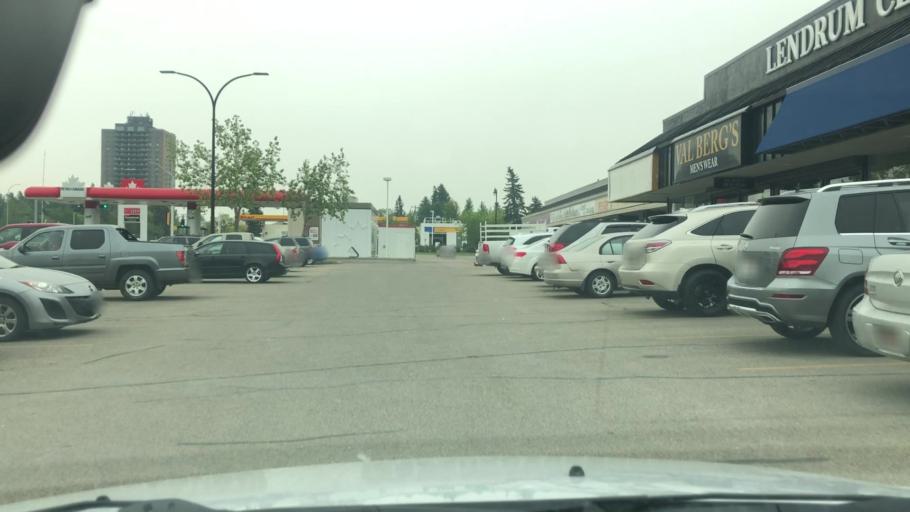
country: CA
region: Alberta
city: Edmonton
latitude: 53.4952
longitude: -113.5174
